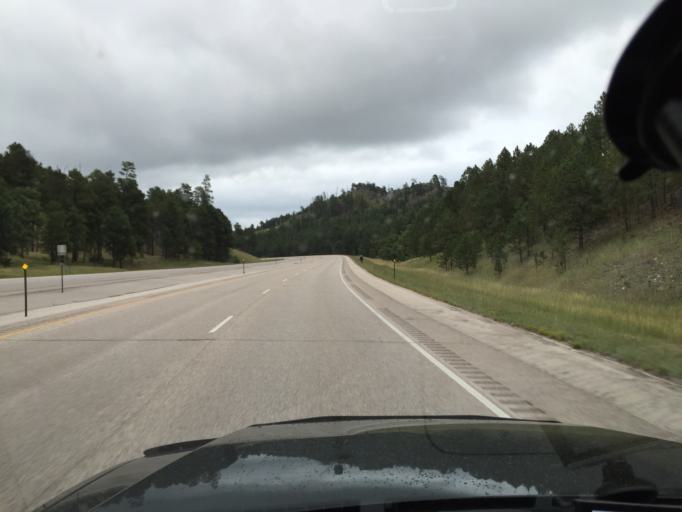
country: US
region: South Dakota
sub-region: Pennington County
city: Colonial Pine Hills
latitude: 43.9398
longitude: -103.4092
